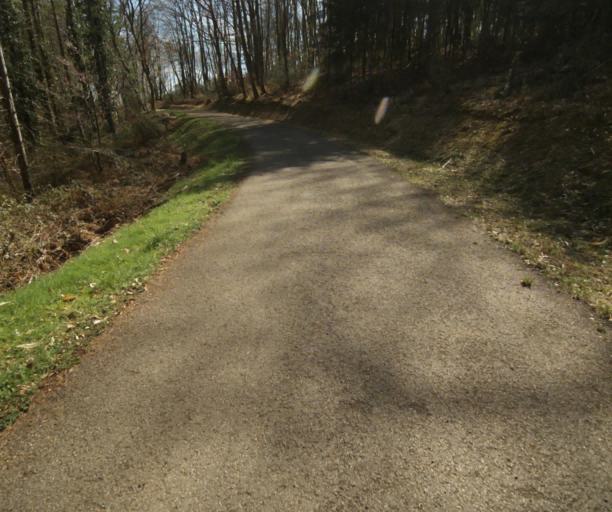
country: FR
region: Limousin
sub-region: Departement de la Correze
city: Seilhac
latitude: 45.3997
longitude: 1.7763
